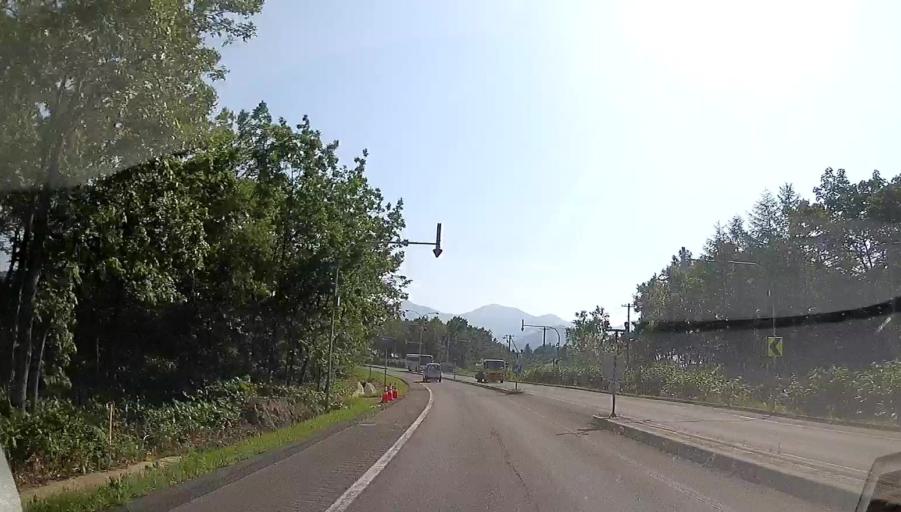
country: JP
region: Hokkaido
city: Otofuke
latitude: 42.9884
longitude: 142.8406
